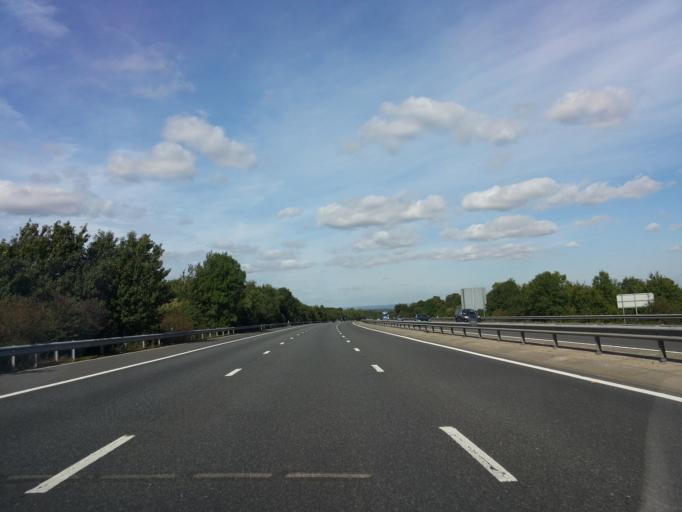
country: GB
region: England
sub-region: Kent
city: Borough Green
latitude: 51.3288
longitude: 0.2735
